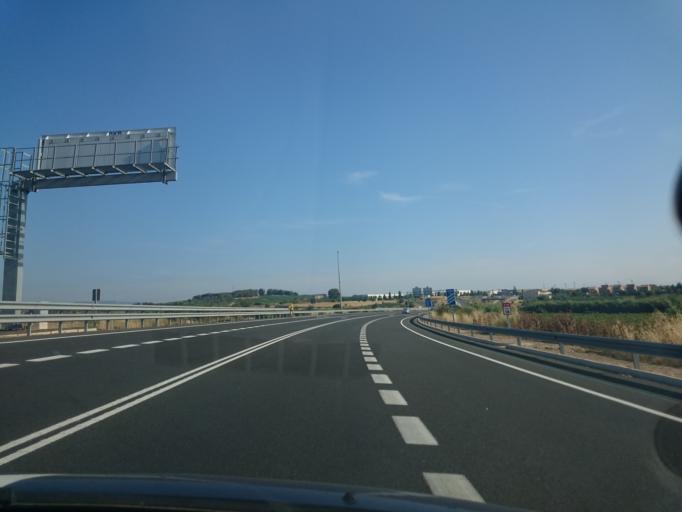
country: ES
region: Catalonia
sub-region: Provincia de Barcelona
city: La Granada
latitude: 41.3709
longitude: 1.7112
